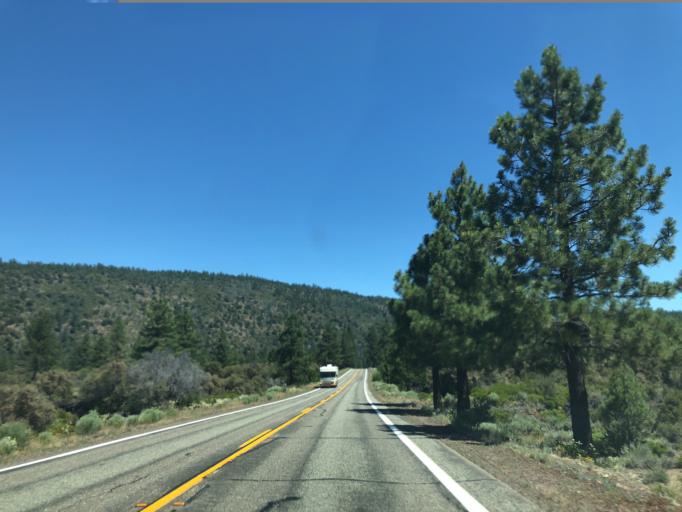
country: US
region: California
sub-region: Shasta County
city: Burney
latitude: 40.6790
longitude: -121.4157
